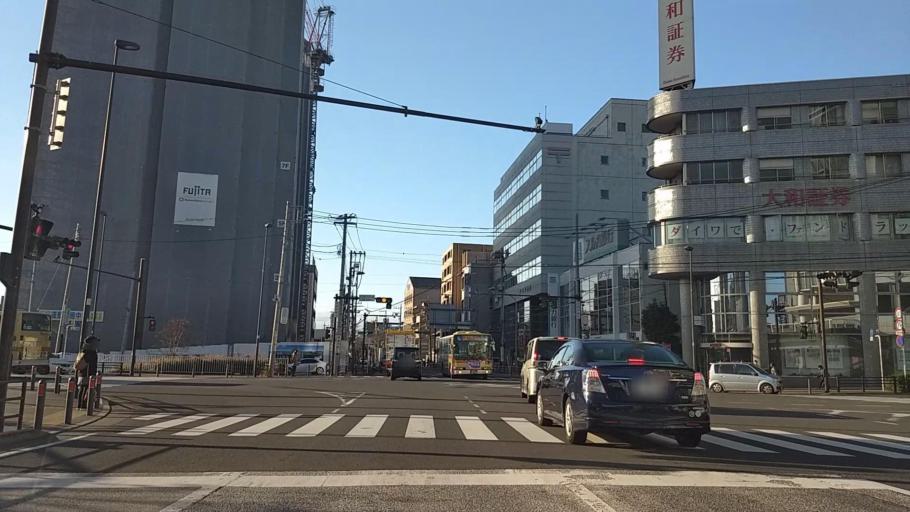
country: JP
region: Kanagawa
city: Fujisawa
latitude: 35.4009
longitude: 139.5319
